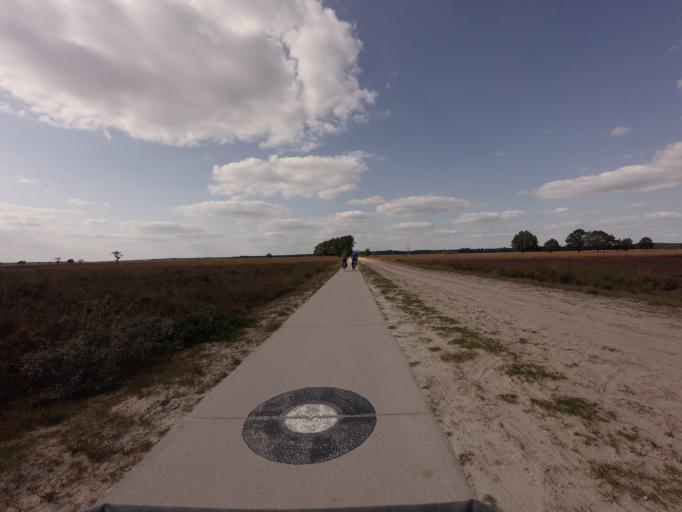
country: NL
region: Drenthe
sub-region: Gemeente Westerveld
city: Dwingeloo
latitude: 52.7986
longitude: 6.4253
